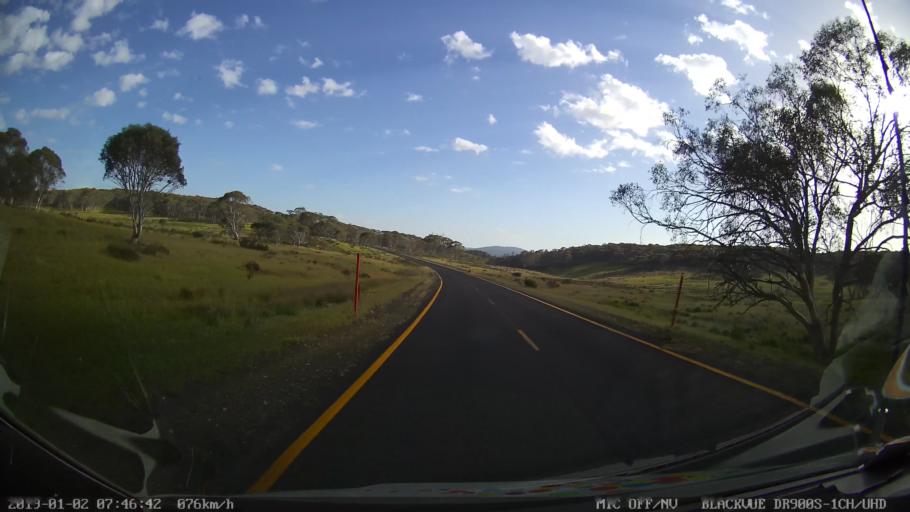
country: AU
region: New South Wales
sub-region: Tumut Shire
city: Tumut
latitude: -35.7726
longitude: 148.5193
